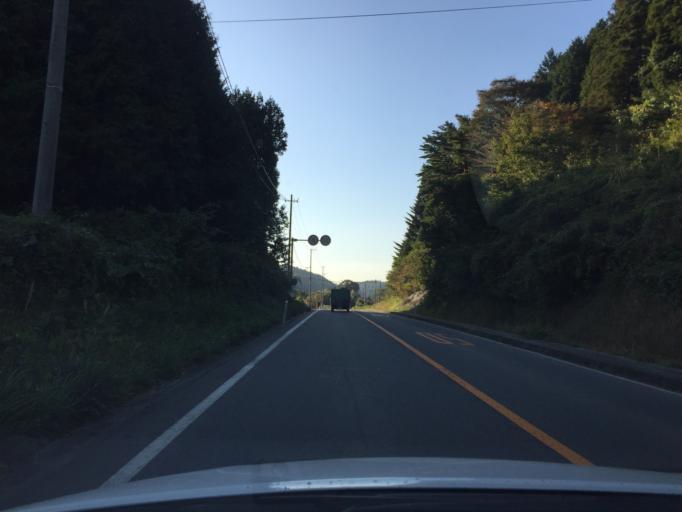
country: JP
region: Fukushima
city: Iwaki
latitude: 37.1171
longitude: 140.7508
